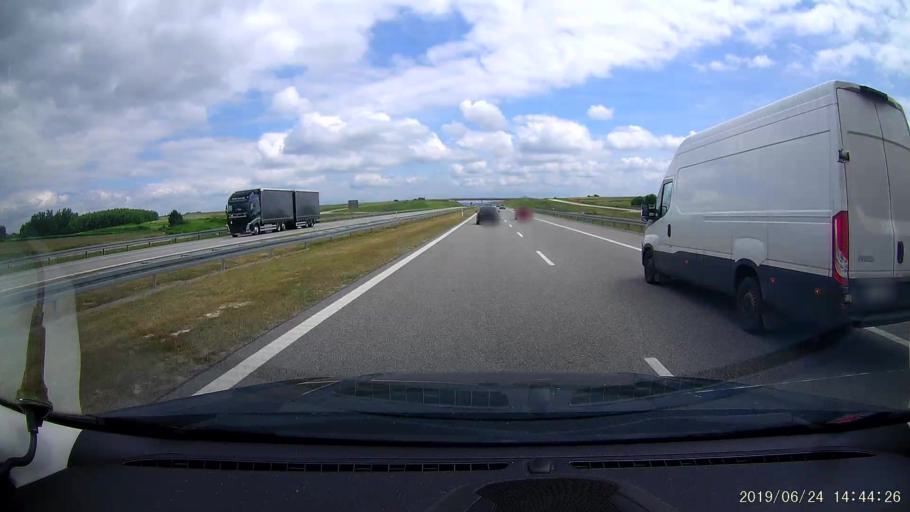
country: PL
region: Subcarpathian Voivodeship
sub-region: Powiat debicki
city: Czarna
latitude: 50.0947
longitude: 21.2933
